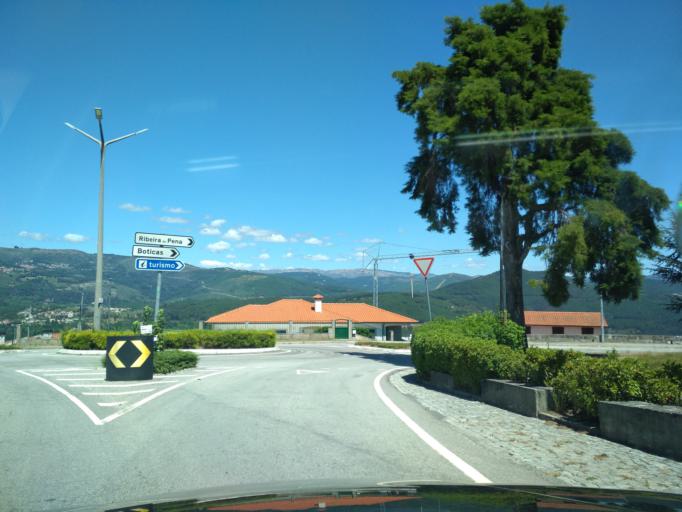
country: PT
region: Vila Real
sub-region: Ribeira de Pena
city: Ribeira de Pena
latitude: 41.5202
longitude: -7.8073
